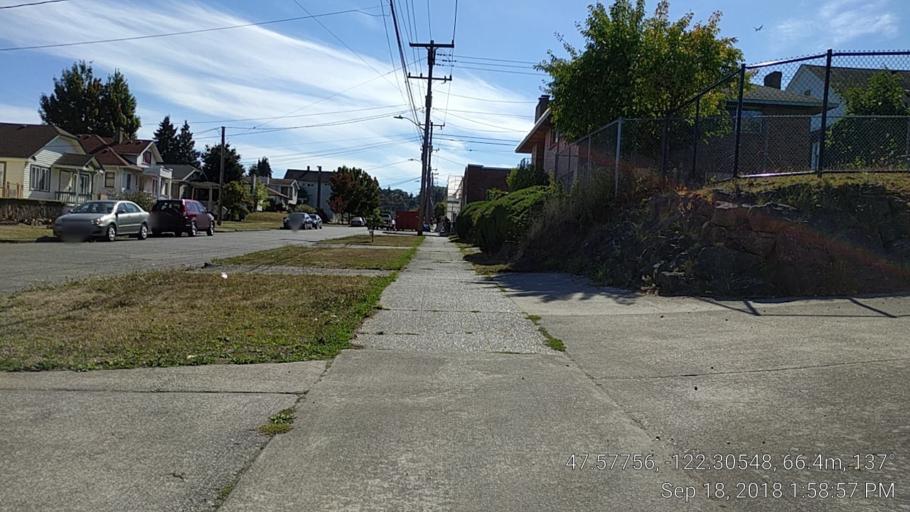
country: US
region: Washington
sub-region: King County
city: Seattle
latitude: 47.5776
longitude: -122.3055
